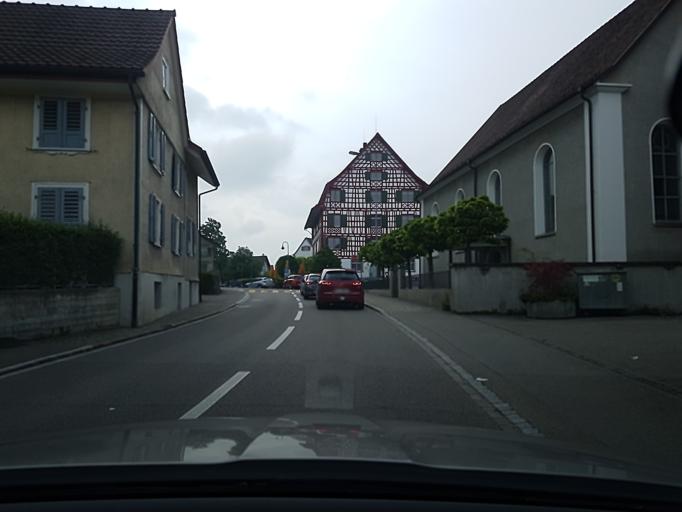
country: CH
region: Thurgau
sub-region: Arbon District
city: Roggwil
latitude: 47.4999
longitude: 9.3966
